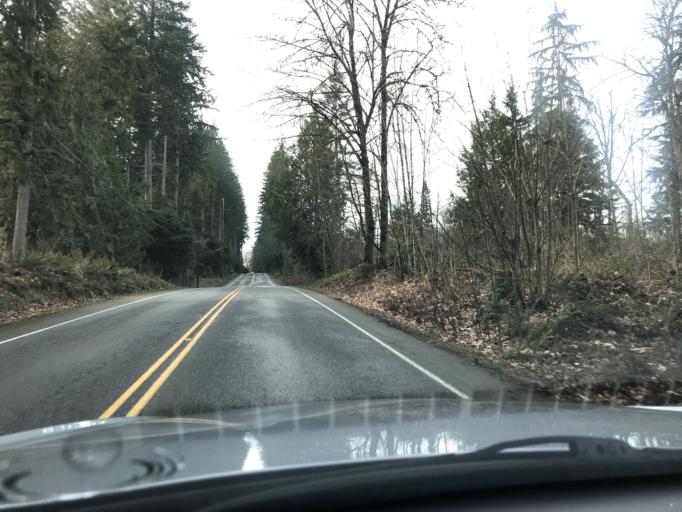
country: US
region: Washington
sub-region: King County
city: Ames Lake
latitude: 47.6529
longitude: -121.9783
